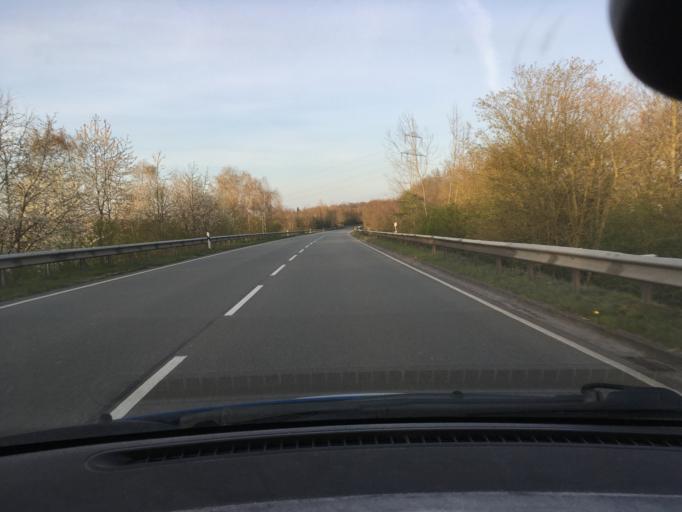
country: DE
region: Lower Saxony
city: Melbeck
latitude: 53.1972
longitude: 10.3802
